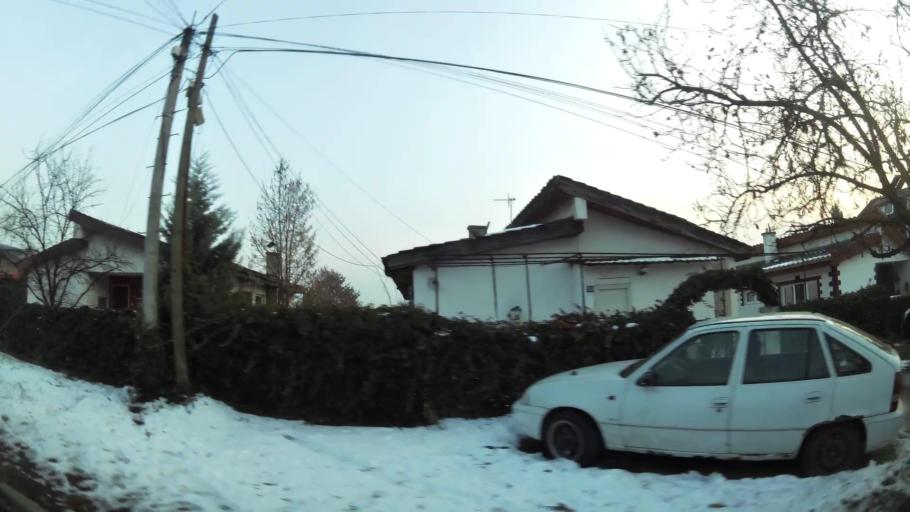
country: MK
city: Creshevo
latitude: 42.0103
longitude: 21.5063
